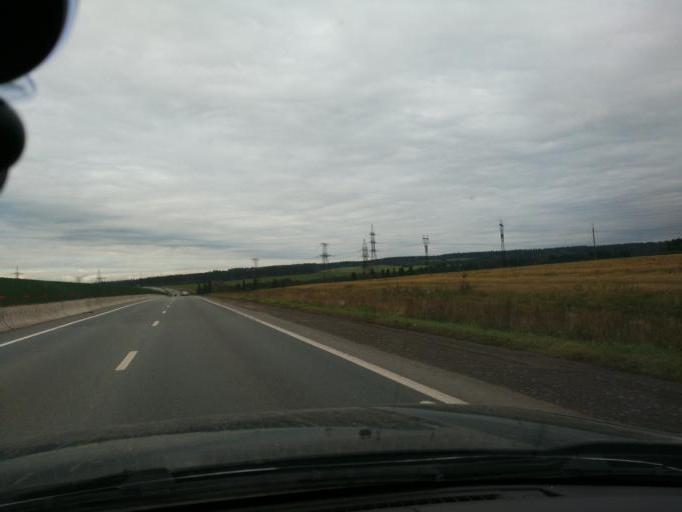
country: RU
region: Perm
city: Ferma
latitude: 57.9353
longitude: 56.3582
